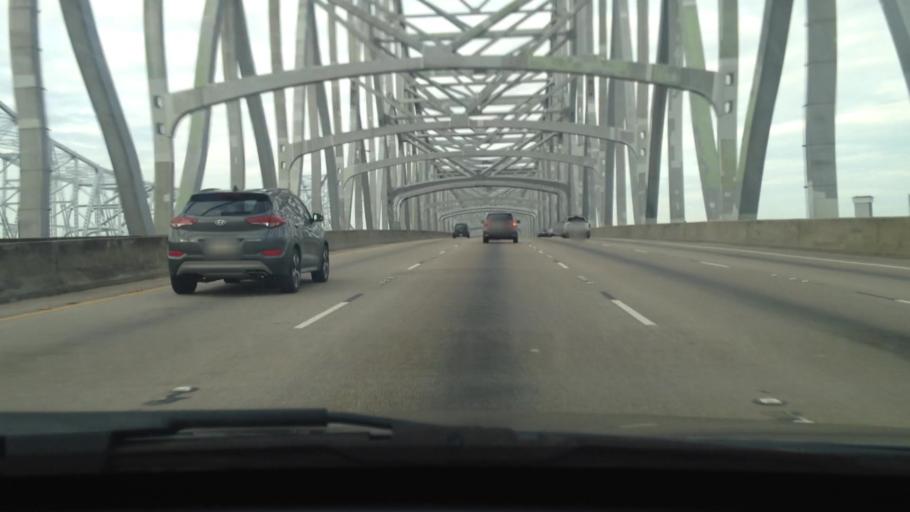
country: US
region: Louisiana
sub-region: Jefferson Parish
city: Gretna
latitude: 29.9388
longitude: -90.0523
